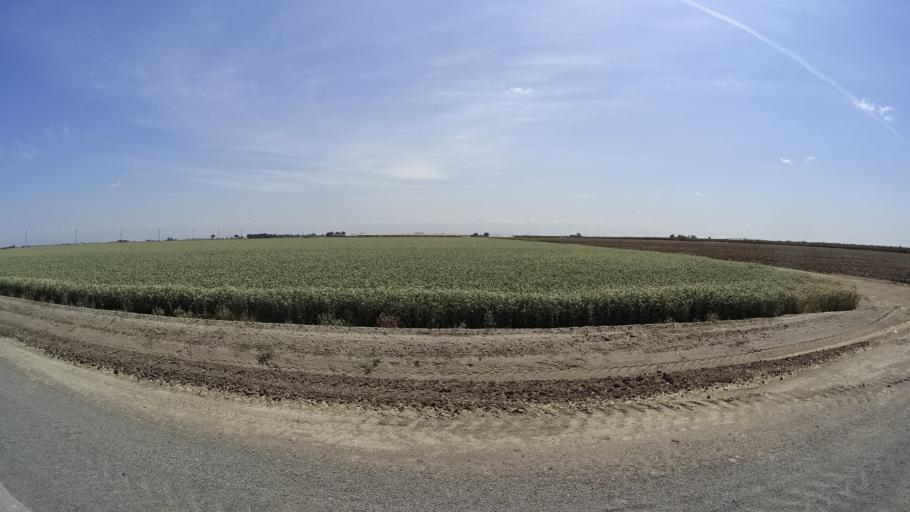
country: US
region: California
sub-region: Tulare County
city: Goshen
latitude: 36.2799
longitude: -119.4922
